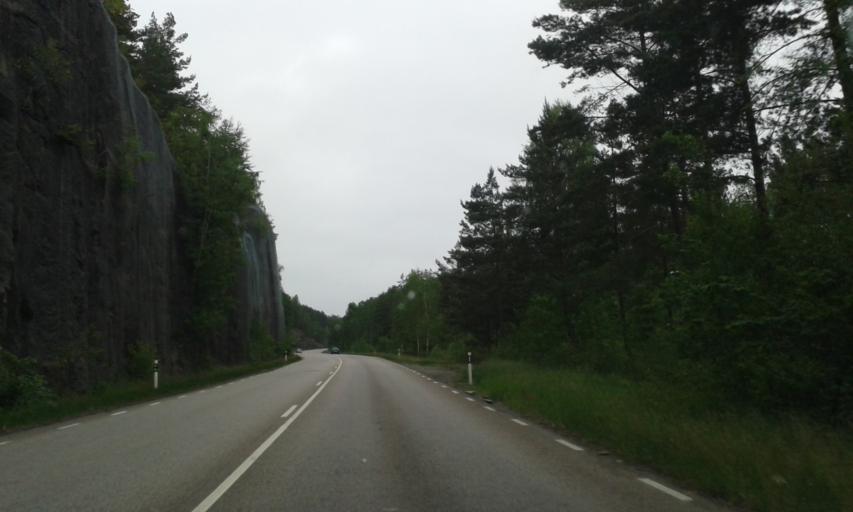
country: SE
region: Vaestra Goetaland
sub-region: Partille Kommun
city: Partille
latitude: 57.7430
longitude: 12.0786
